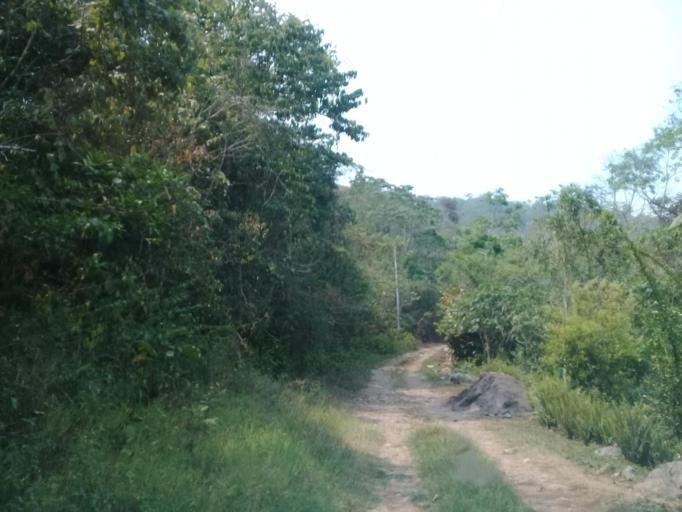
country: MX
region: Veracruz
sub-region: Tezonapa
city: Laguna Chica (Pueblo Nuevo)
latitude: 18.5826
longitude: -96.7499
